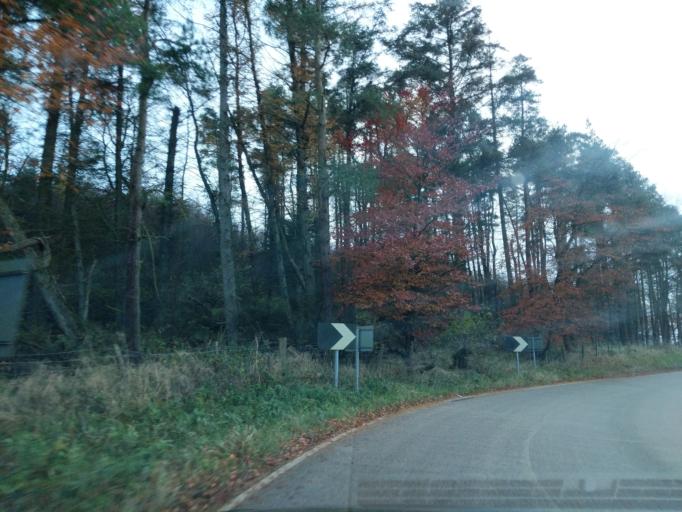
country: GB
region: Scotland
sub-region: West Lothian
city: Linlithgow
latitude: 55.9452
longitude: -3.6159
